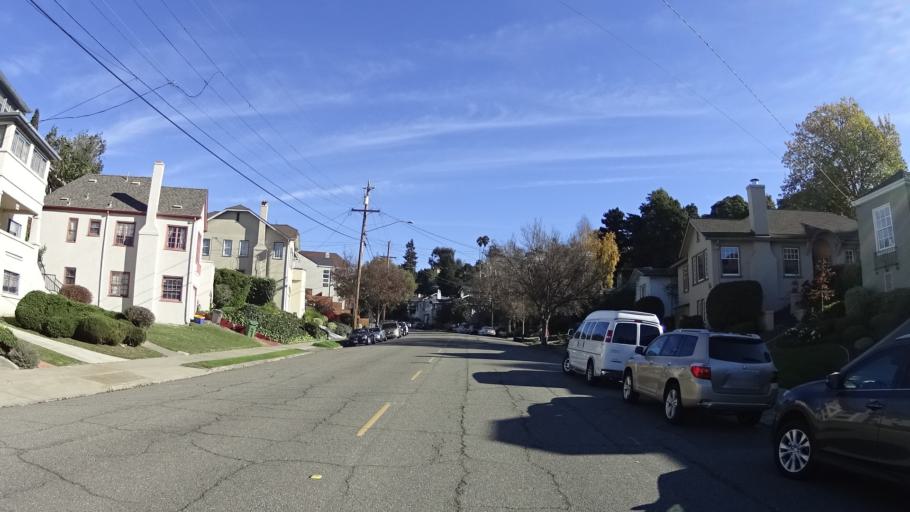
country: US
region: California
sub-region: Alameda County
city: Piedmont
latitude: 37.8146
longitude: -122.2368
